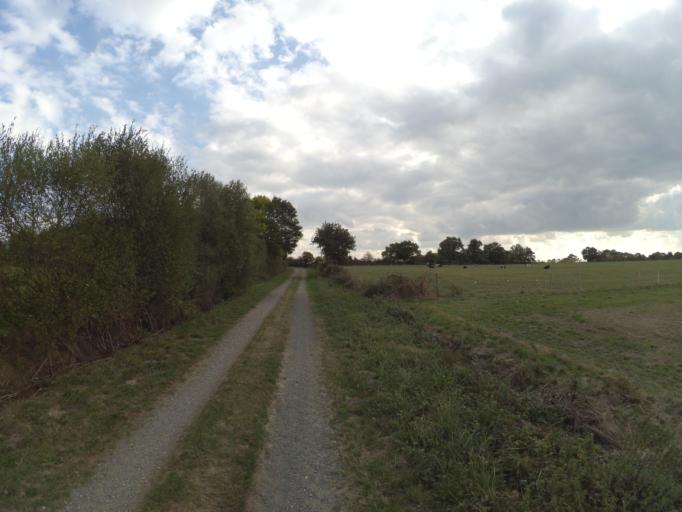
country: FR
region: Pays de la Loire
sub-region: Departement de la Loire-Atlantique
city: Saint-Lumine-de-Clisson
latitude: 47.0738
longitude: -1.3326
